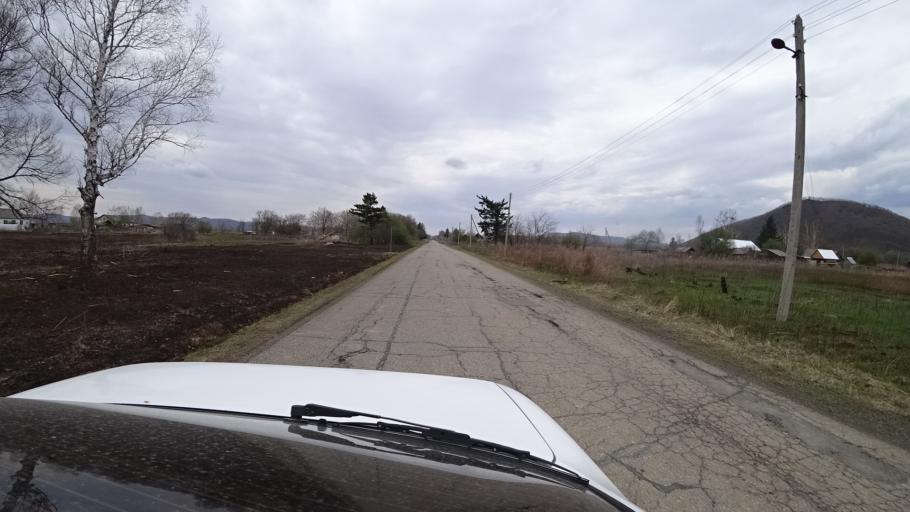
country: RU
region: Primorskiy
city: Novopokrovka
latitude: 45.5739
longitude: 134.3178
